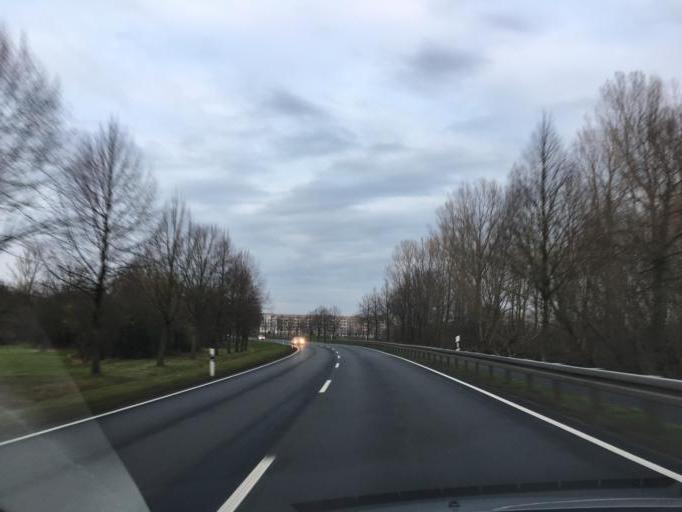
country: DE
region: Saxony
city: Borna
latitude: 51.1073
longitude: 12.4896
